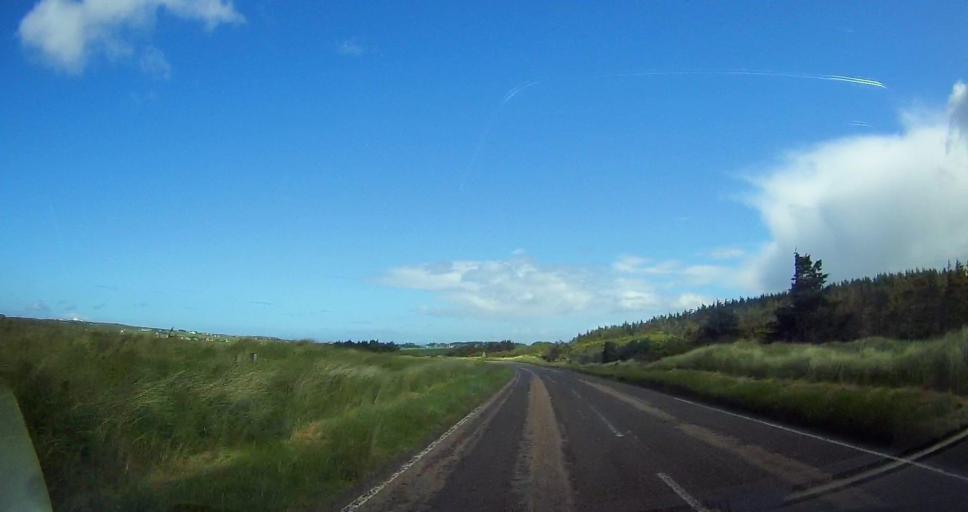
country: GB
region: Scotland
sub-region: Highland
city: Thurso
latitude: 58.6097
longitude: -3.3434
